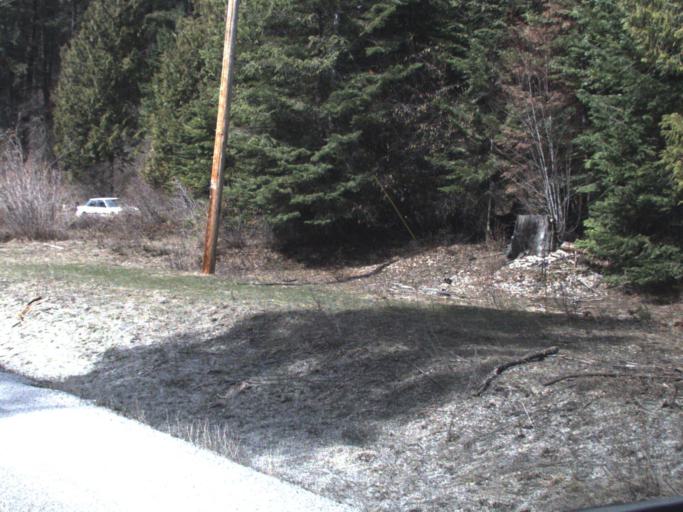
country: US
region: Washington
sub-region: Pend Oreille County
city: Newport
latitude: 48.4718
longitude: -117.3097
